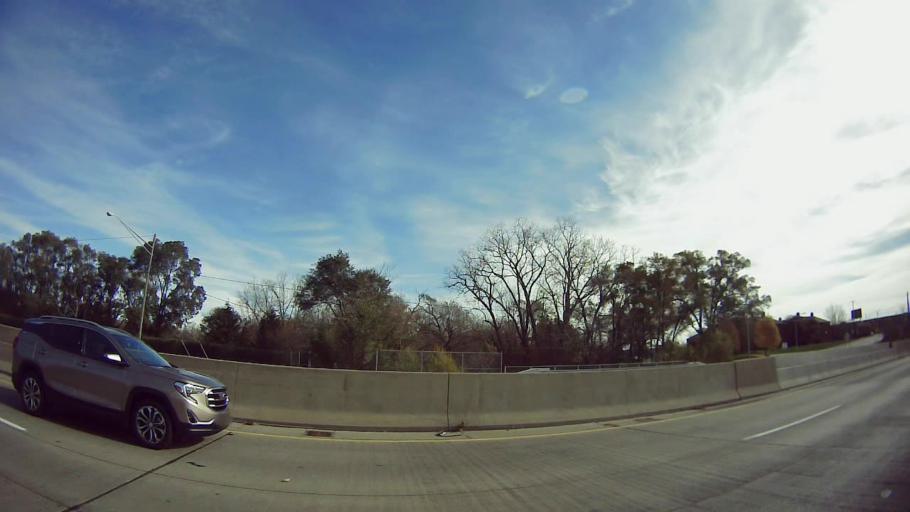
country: US
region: Michigan
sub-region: Wayne County
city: Dearborn Heights
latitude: 42.3017
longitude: -83.2721
